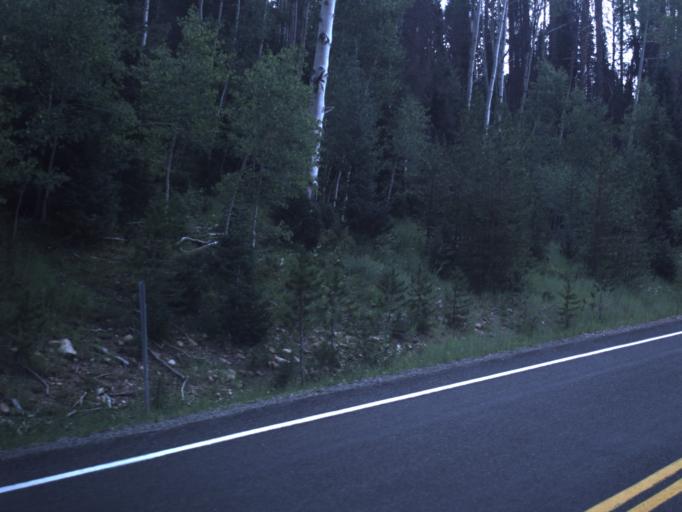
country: US
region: Utah
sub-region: Summit County
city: Francis
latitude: 40.5174
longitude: -111.0473
